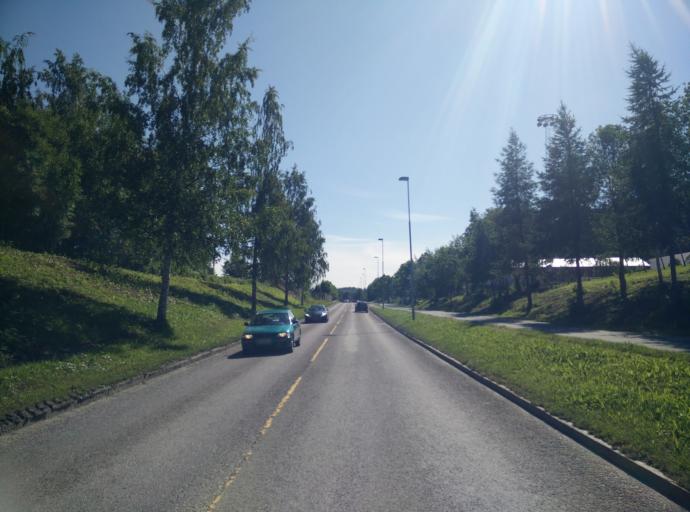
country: NO
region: Sor-Trondelag
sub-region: Trondheim
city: Trondheim
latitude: 63.3937
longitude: 10.3497
